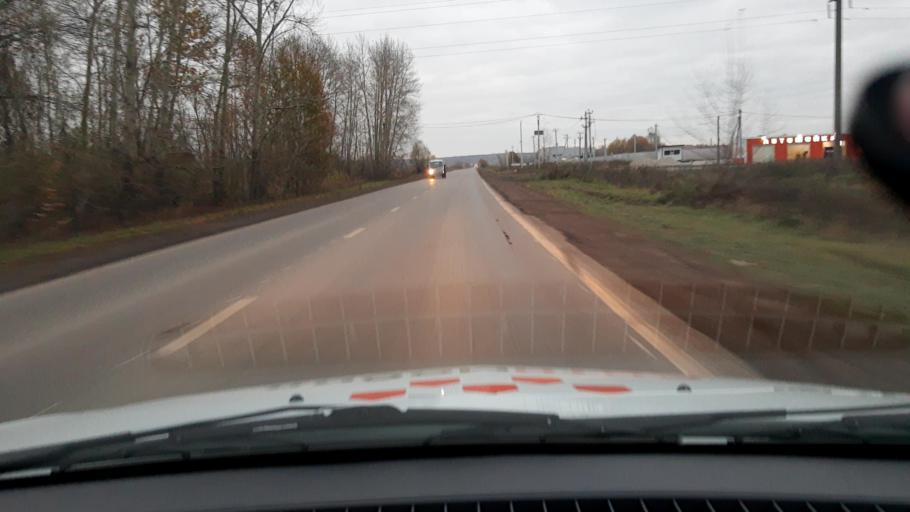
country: RU
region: Bashkortostan
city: Kabakovo
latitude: 54.6793
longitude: 56.1051
